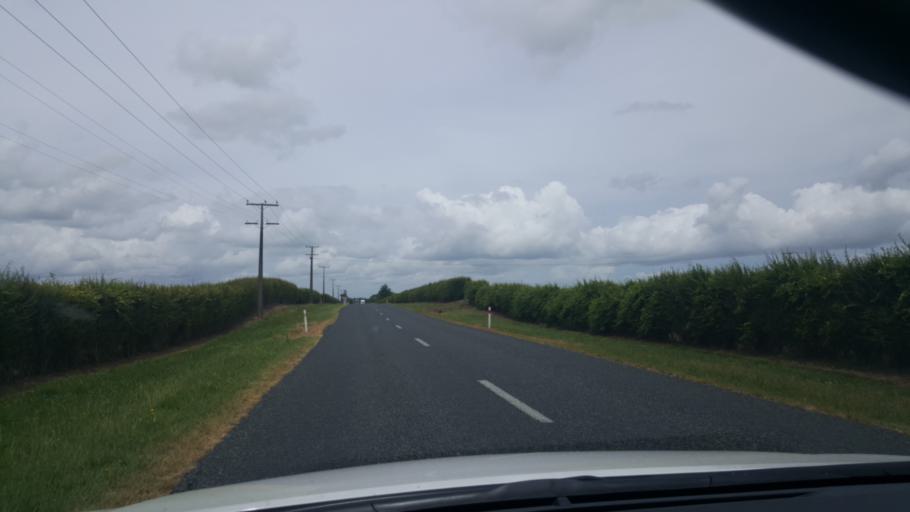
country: NZ
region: Waikato
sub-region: Matamata-Piako District
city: Matamata
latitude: -37.8787
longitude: 175.7288
